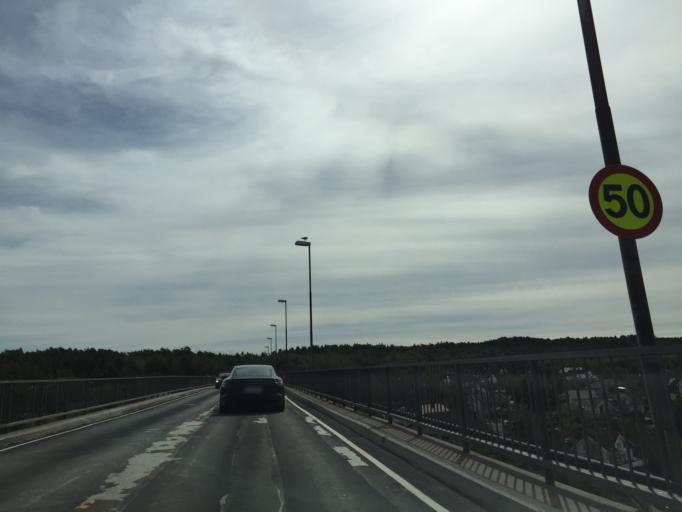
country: NO
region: Ostfold
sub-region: Fredrikstad
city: Fredrikstad
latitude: 59.1461
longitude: 10.9437
